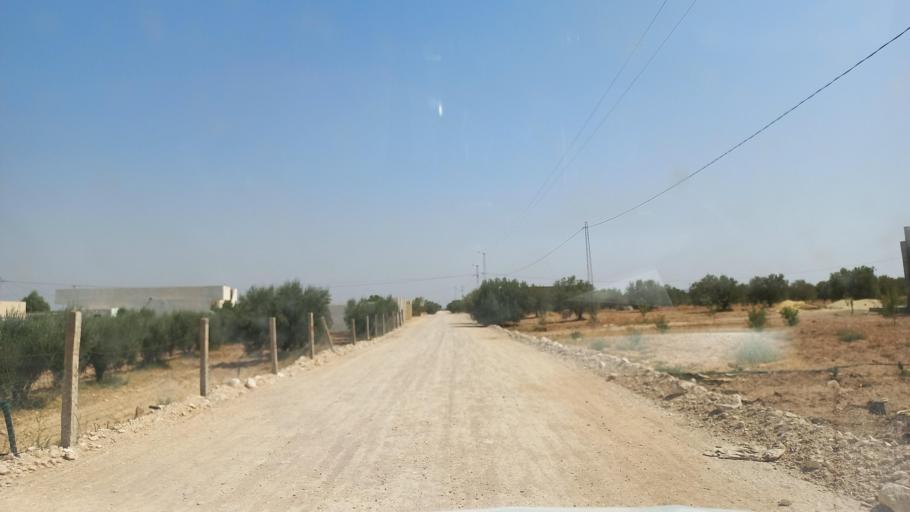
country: TN
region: Al Qasrayn
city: Kasserine
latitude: 35.2597
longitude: 9.0112
